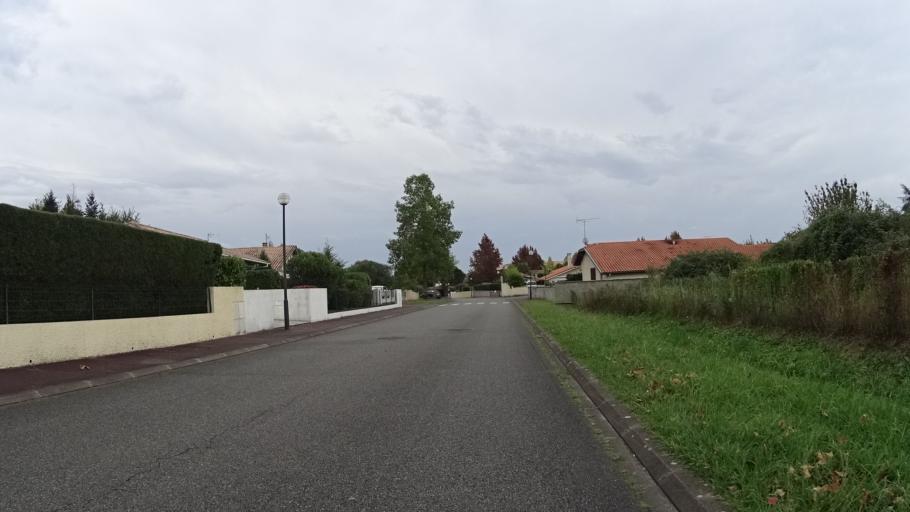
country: FR
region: Aquitaine
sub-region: Departement des Landes
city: Saint-Paul-les-Dax
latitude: 43.7295
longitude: -1.0799
